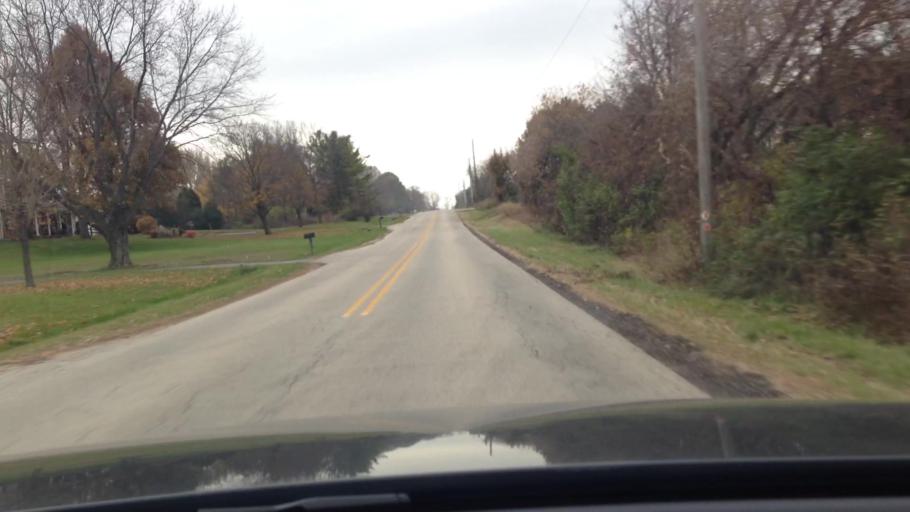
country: US
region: Illinois
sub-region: McHenry County
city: Woodstock
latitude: 42.2829
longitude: -88.4770
